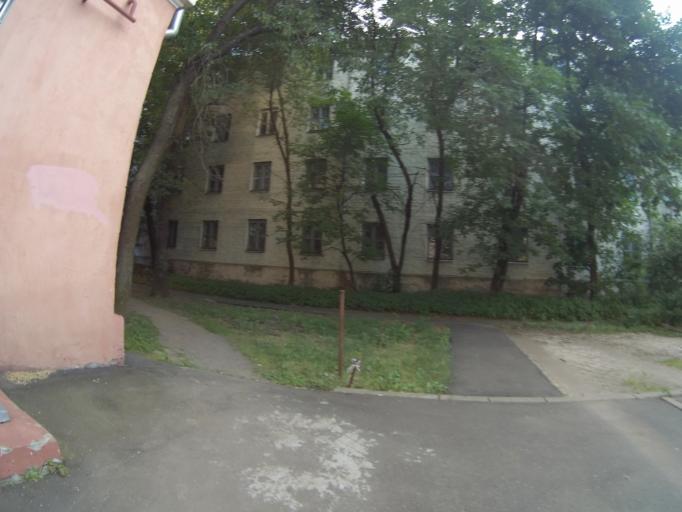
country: RU
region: Vladimir
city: Vladimir
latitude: 56.1344
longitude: 40.4210
